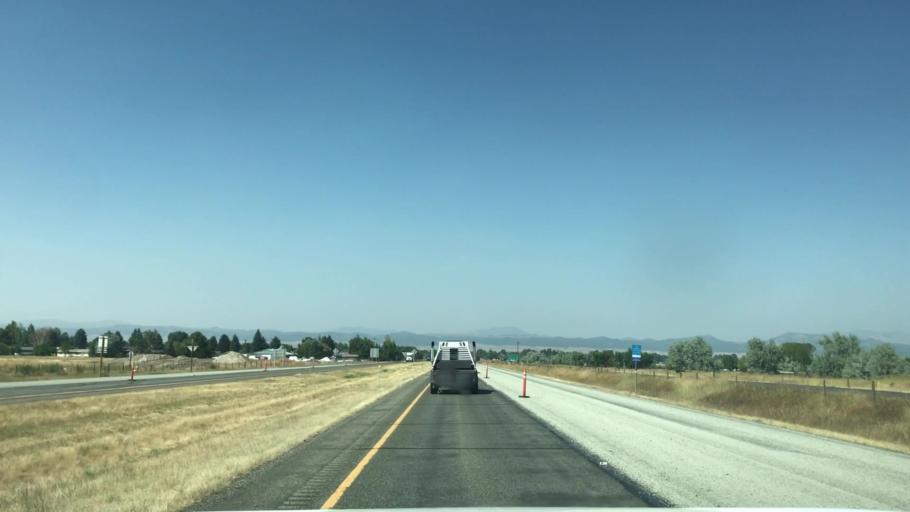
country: US
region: Montana
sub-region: Lewis and Clark County
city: Helena
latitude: 46.6271
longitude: -112.0109
